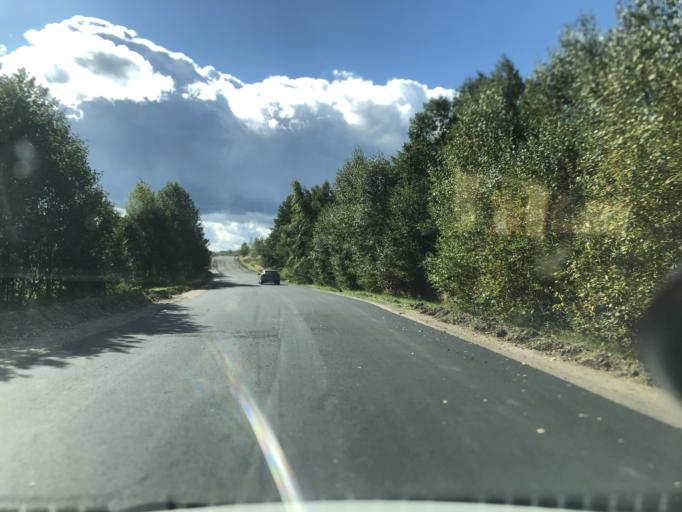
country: RU
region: Jaroslavl
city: Porech'ye-Rybnoye
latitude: 56.9703
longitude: 39.3917
